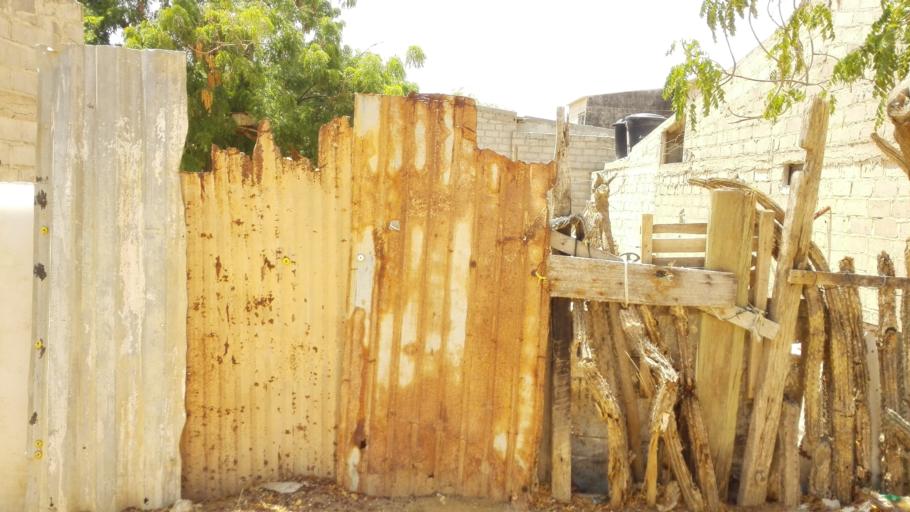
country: CO
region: La Guajira
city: Manaure
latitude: 11.7731
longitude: -72.4455
